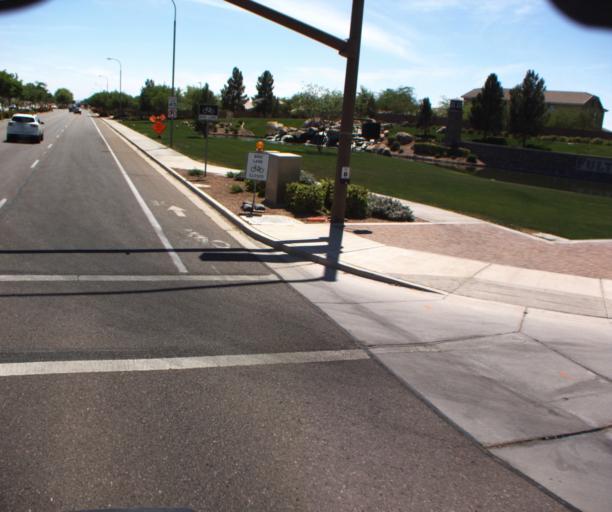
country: US
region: Arizona
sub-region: Maricopa County
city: Sun Lakes
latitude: 33.2403
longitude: -111.8413
